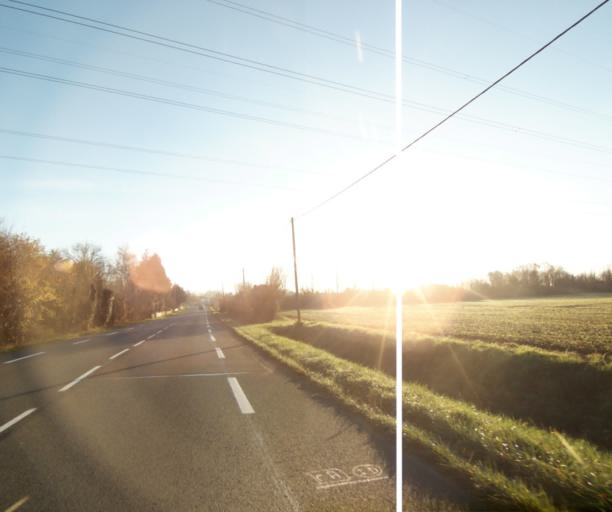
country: FR
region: Poitou-Charentes
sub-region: Departement de la Charente-Maritime
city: Fontcouverte
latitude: 45.7453
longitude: -0.5807
